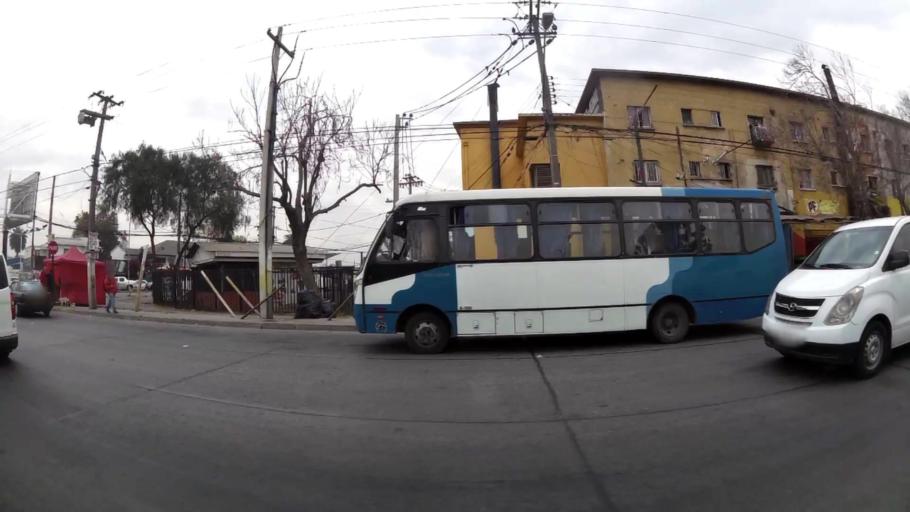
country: CL
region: Santiago Metropolitan
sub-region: Provincia de Santiago
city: Santiago
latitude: -33.4144
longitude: -70.6788
